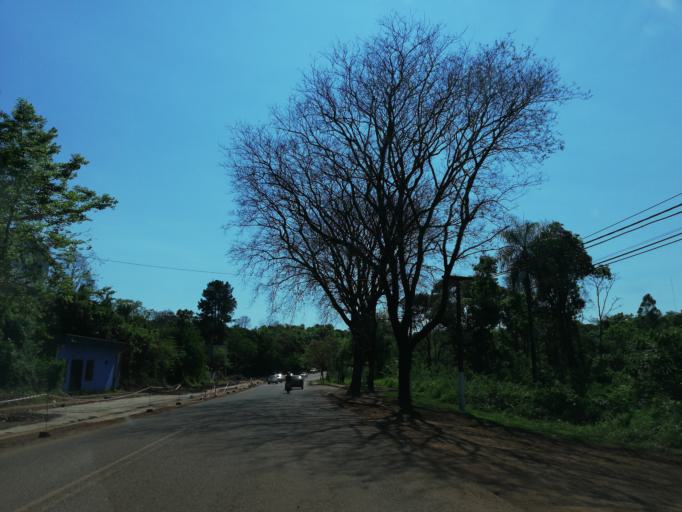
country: AR
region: Misiones
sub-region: Departamento de Eldorado
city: Eldorado
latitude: -26.4052
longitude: -54.6395
